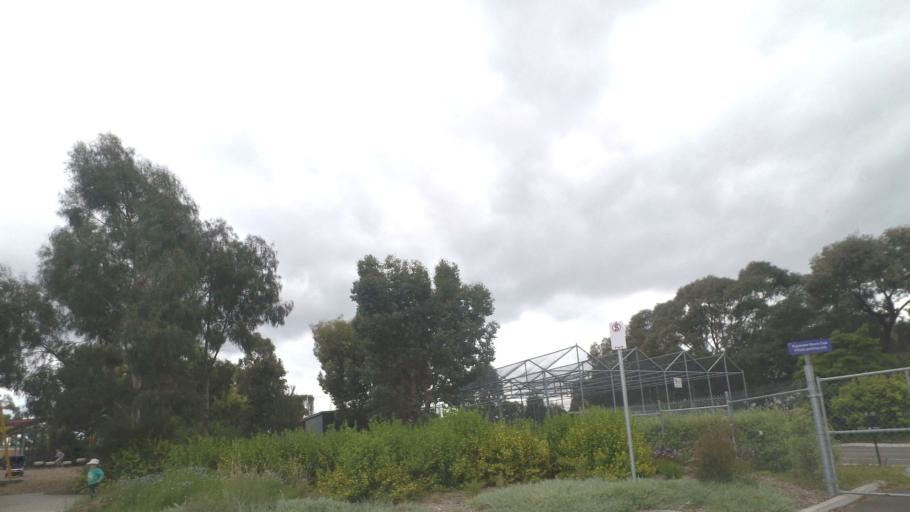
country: AU
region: Victoria
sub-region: Knox
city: Bayswater
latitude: -37.8480
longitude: 145.2527
